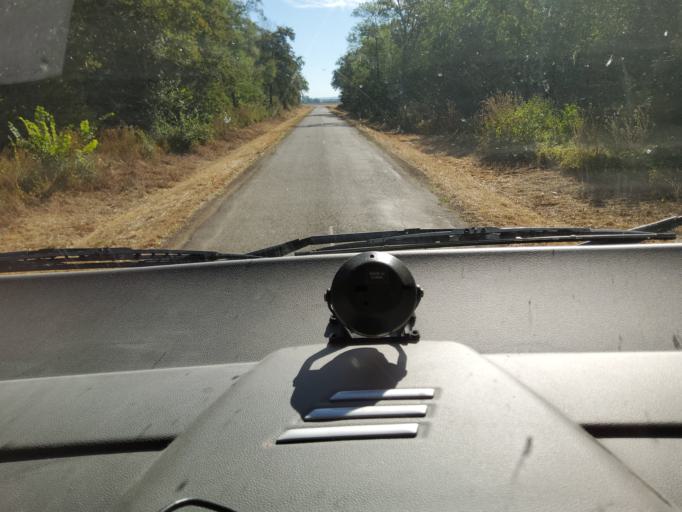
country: FR
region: Bourgogne
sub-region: Departement de la Cote-d'Or
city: Saint-Jean-de-Losne
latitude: 47.1372
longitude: 5.3175
